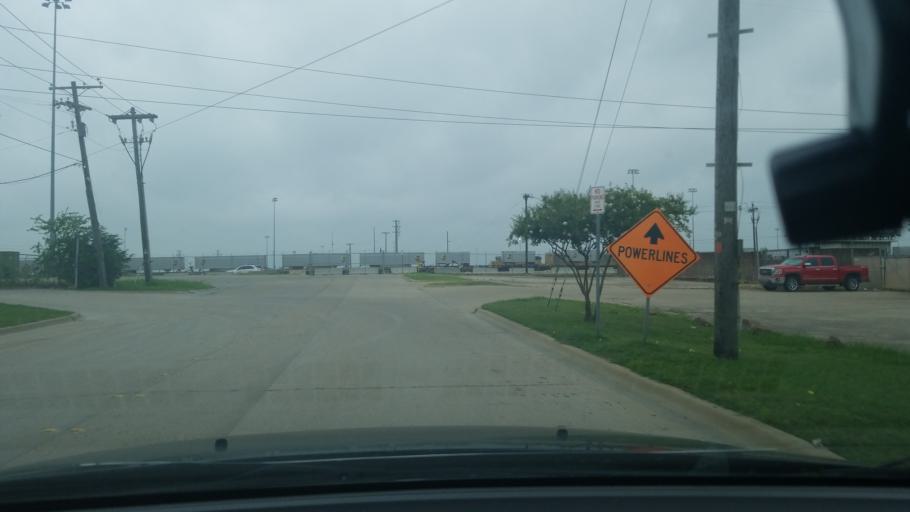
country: US
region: Texas
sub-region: Dallas County
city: Mesquite
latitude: 32.7834
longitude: -96.6587
